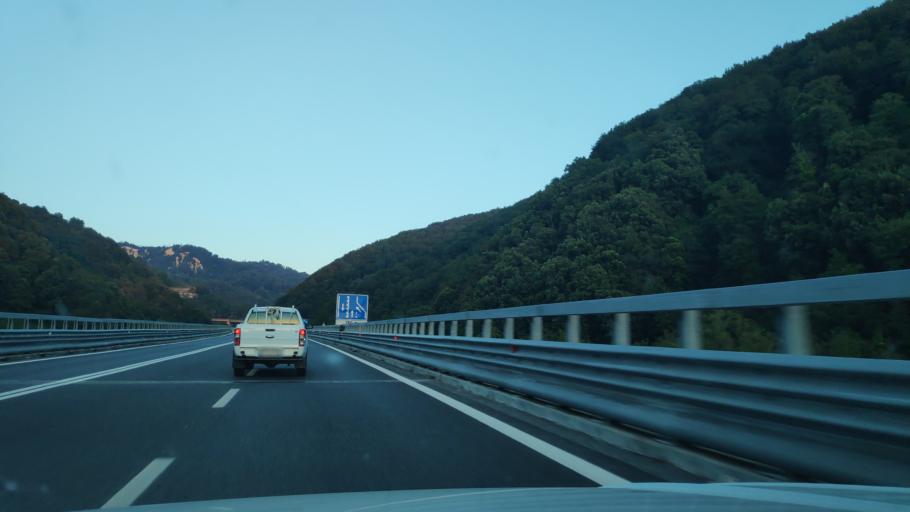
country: IT
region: Calabria
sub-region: Provincia di Reggio Calabria
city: Amato
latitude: 38.4054
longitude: 16.1526
